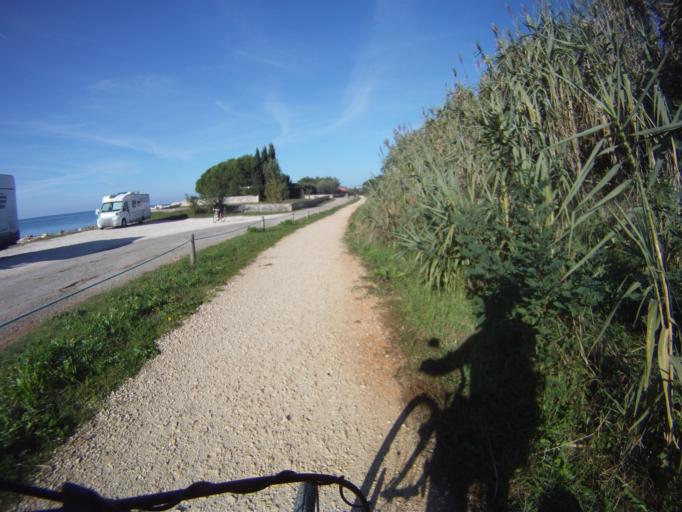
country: HR
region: Istarska
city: Novigrad
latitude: 45.3358
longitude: 13.5427
